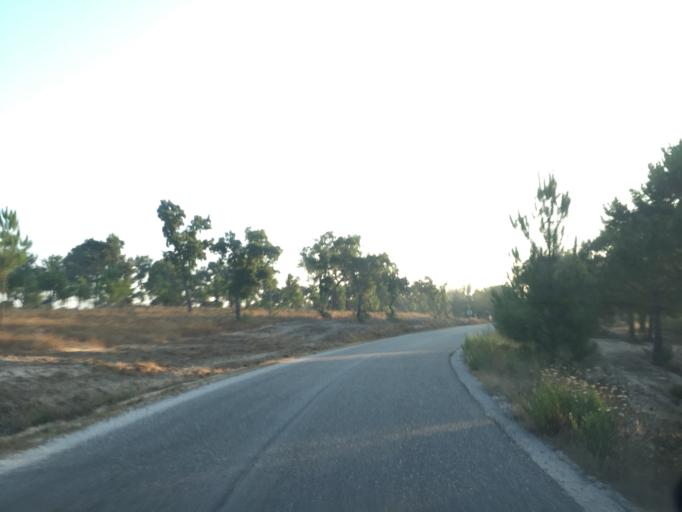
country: PT
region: Santarem
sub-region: Coruche
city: Coruche
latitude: 39.0380
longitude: -8.4429
